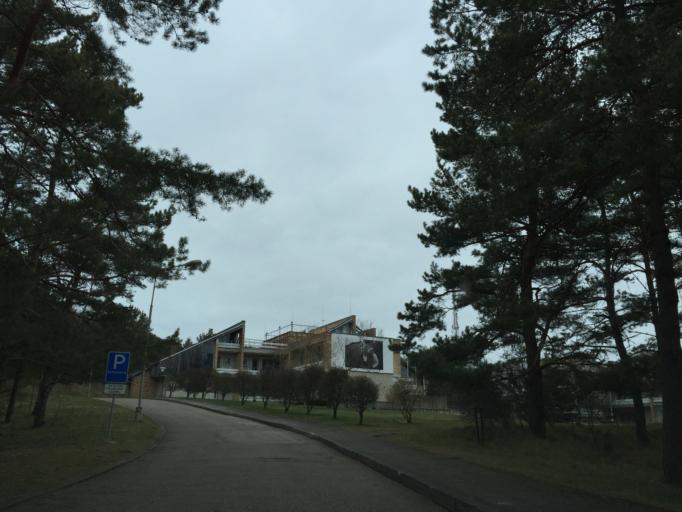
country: LT
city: Nida
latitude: 55.3028
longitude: 20.9972
